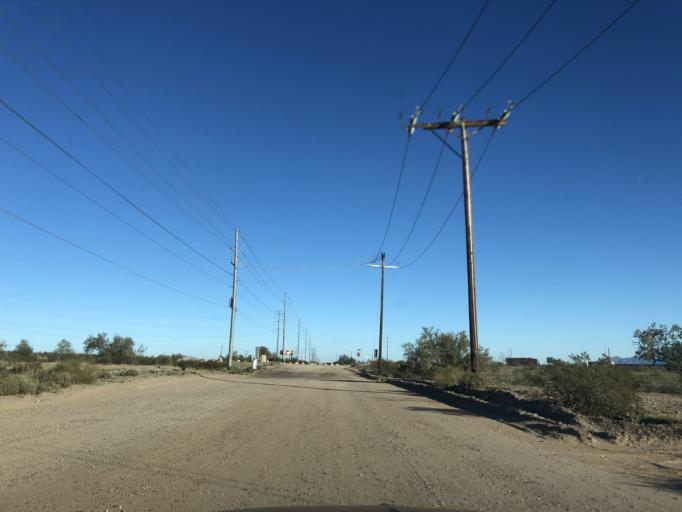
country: US
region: Arizona
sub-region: Maricopa County
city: Buckeye
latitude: 33.4354
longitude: -112.5924
